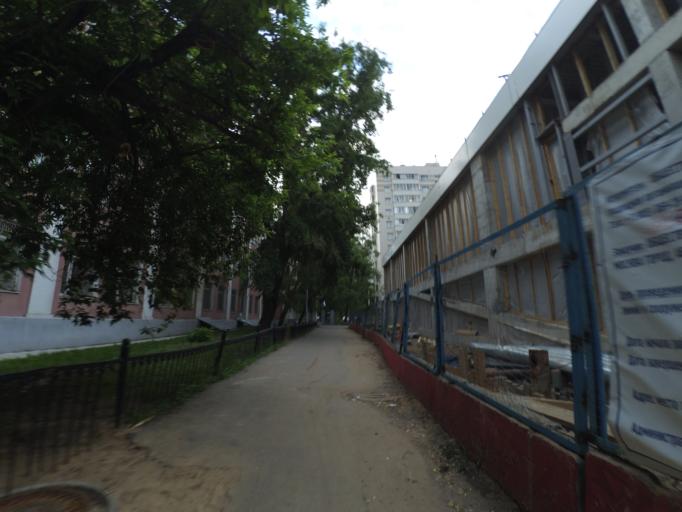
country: RU
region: Moskovskaya
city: Presnenskiy
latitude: 55.7564
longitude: 37.5389
